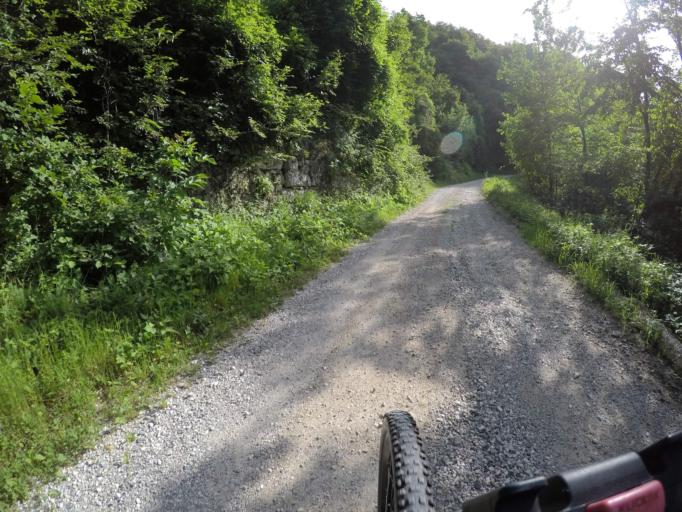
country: IT
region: Friuli Venezia Giulia
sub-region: Provincia di Udine
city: Venzone
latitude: 46.3324
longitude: 13.1831
